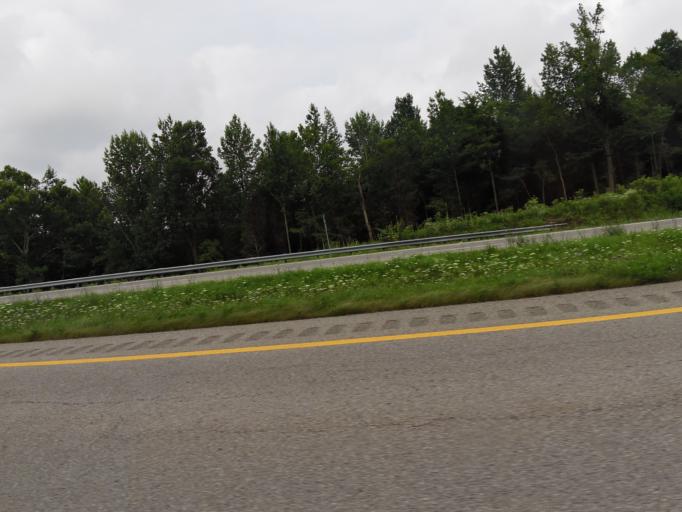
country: US
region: Kentucky
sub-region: Ohio County
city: Beaver Dam
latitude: 37.3359
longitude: -86.9522
